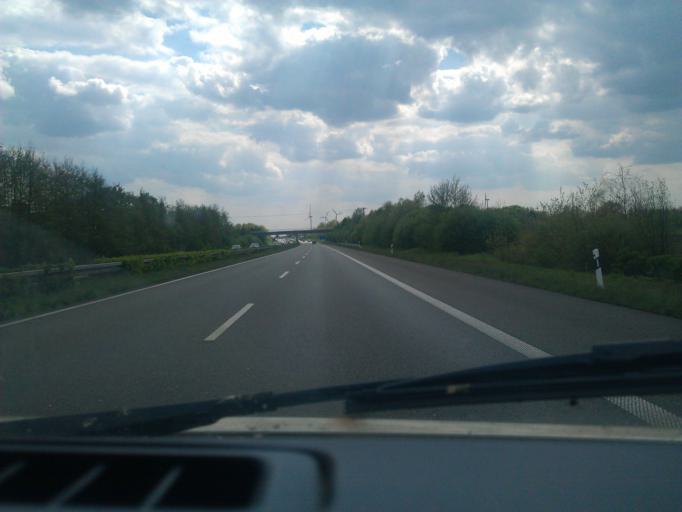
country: DE
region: North Rhine-Westphalia
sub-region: Regierungsbezirk Munster
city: Ochtrup
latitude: 52.2185
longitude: 7.1331
